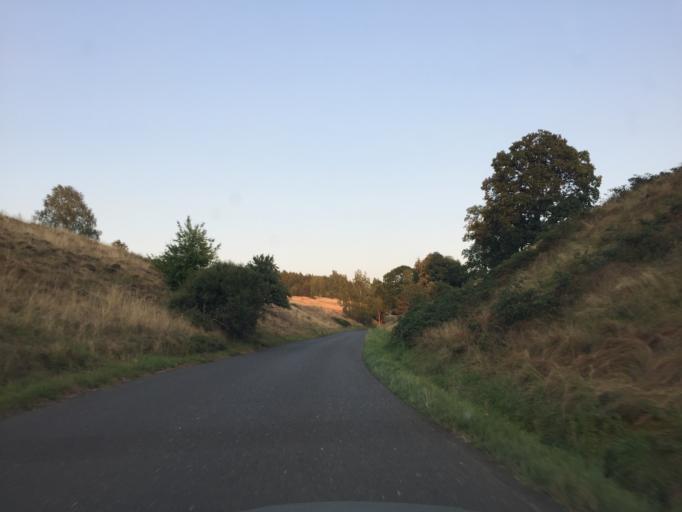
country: CZ
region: Ustecky
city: Ceska Kamenice
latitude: 50.8635
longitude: 14.3492
